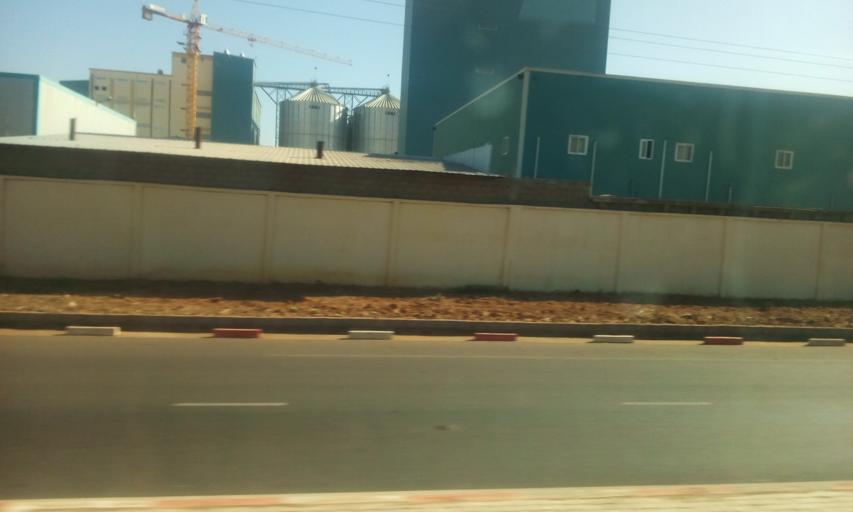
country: ML
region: Segou
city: Segou
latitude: 13.4163
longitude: -6.3126
